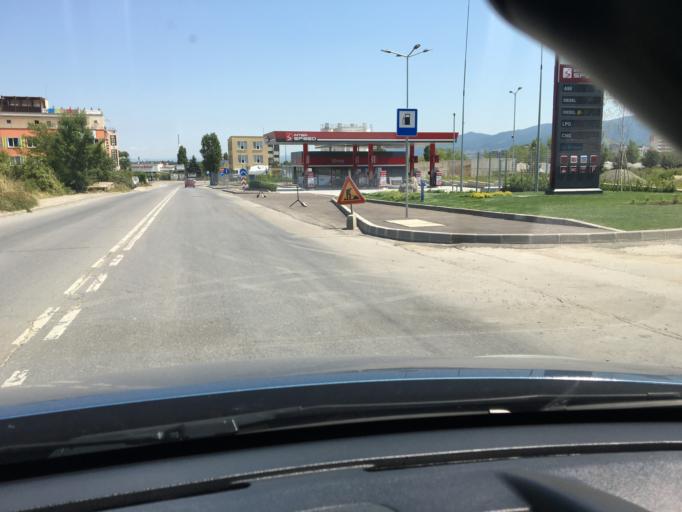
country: BG
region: Sofia-Capital
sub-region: Stolichna Obshtina
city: Sofia
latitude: 42.6387
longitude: 23.3953
